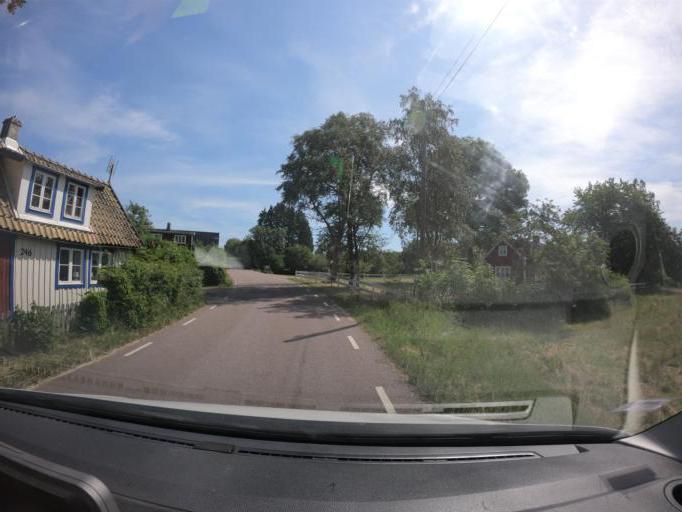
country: SE
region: Skane
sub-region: Bastads Kommun
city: Bastad
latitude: 56.4536
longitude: 12.7152
